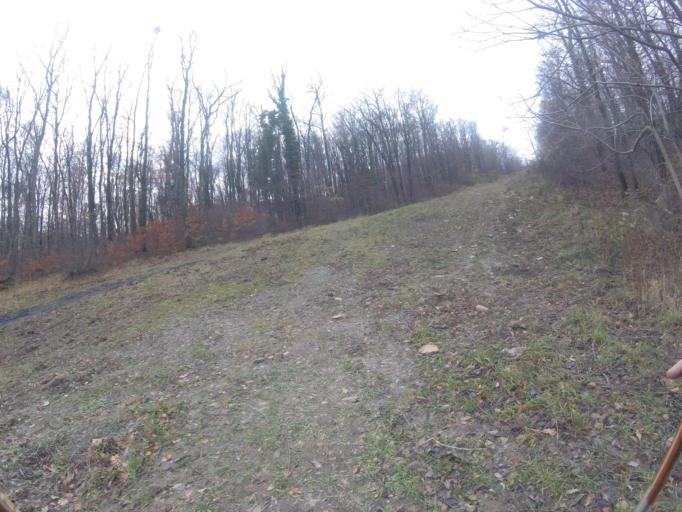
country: HU
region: Veszprem
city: Sumeg
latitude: 46.8913
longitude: 17.3295
